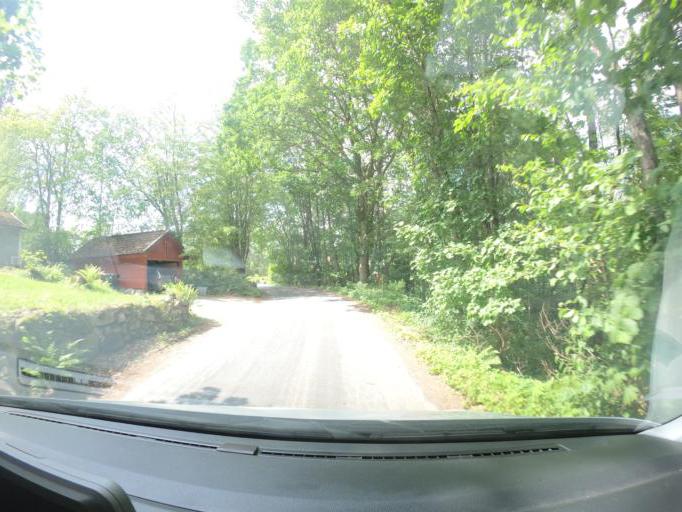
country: SE
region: Skane
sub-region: Hassleholms Kommun
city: Sosdala
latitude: 55.9895
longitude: 13.6301
